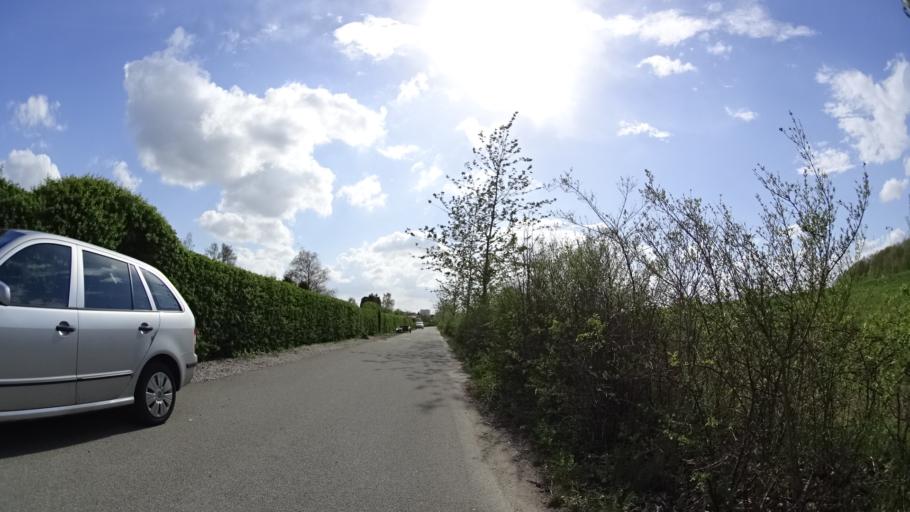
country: DK
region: Central Jutland
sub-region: Arhus Kommune
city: Arhus
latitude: 56.1382
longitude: 10.1672
